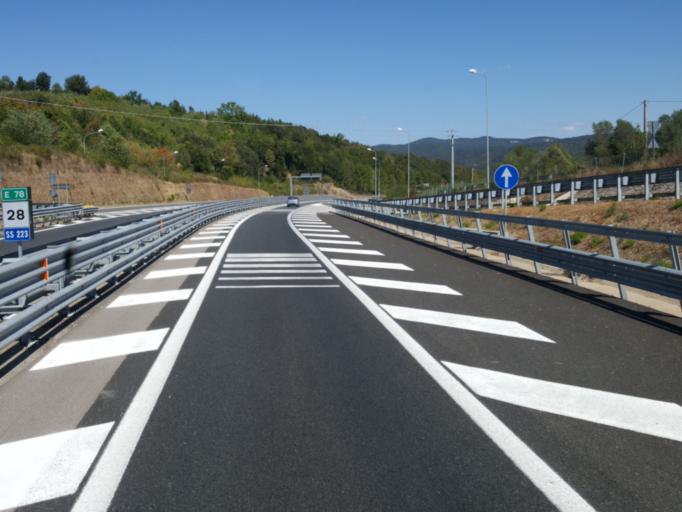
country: IT
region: Tuscany
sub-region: Provincia di Grosseto
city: Civitella Marittima
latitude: 42.9971
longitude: 11.2879
